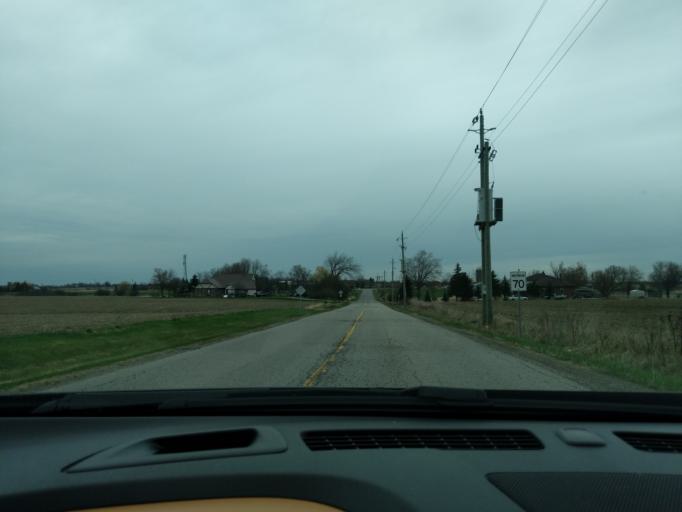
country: CA
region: Ontario
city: Brampton
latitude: 43.8075
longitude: -79.7909
